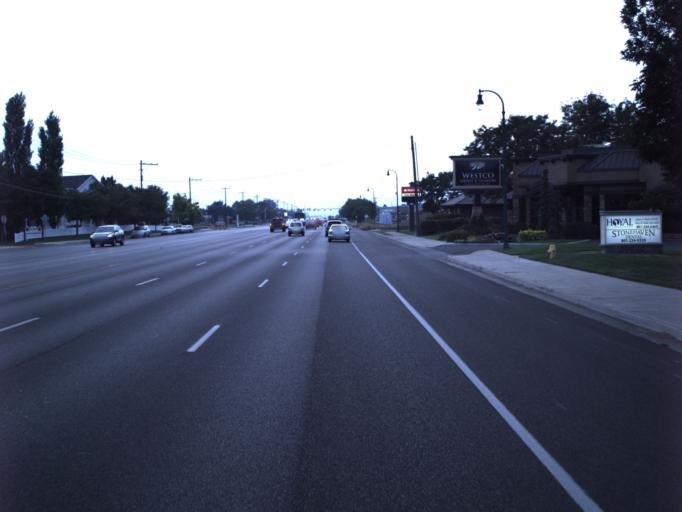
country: US
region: Utah
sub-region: Utah County
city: Lindon
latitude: 40.3299
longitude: -111.7102
